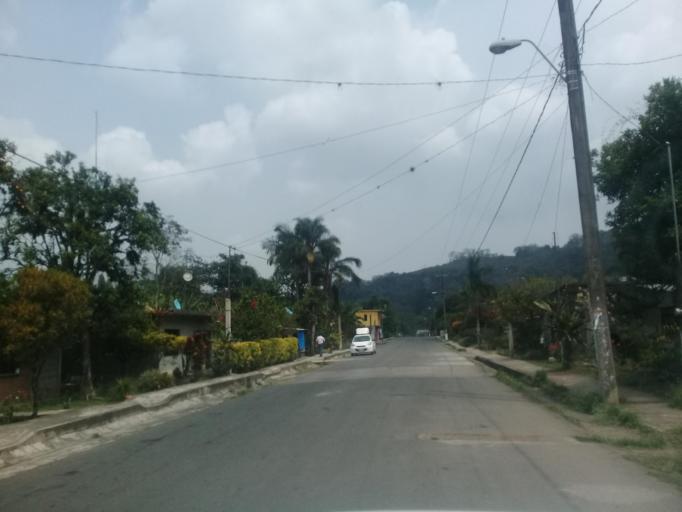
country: MX
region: Veracruz
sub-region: Cordoba
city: San Jose de Tapia
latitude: 18.8230
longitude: -96.9799
